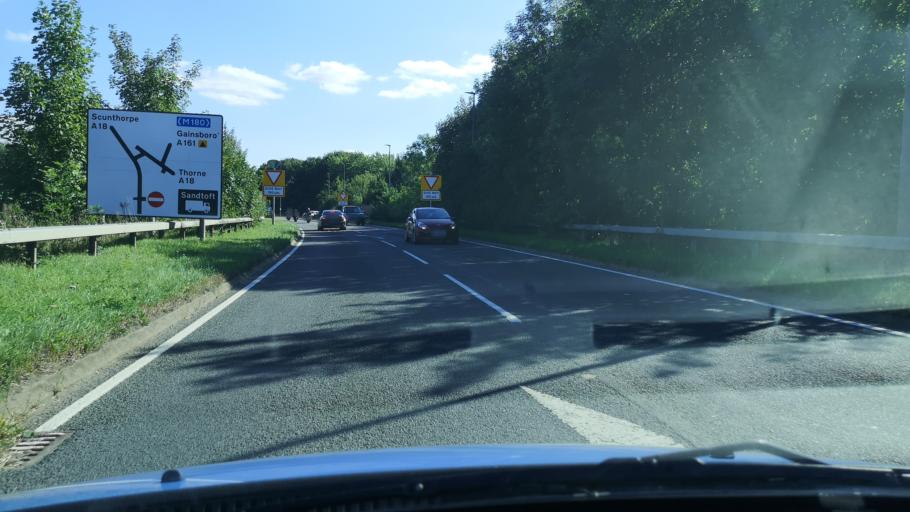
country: GB
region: England
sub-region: North Lincolnshire
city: Crowle
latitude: 53.5876
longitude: -0.8188
